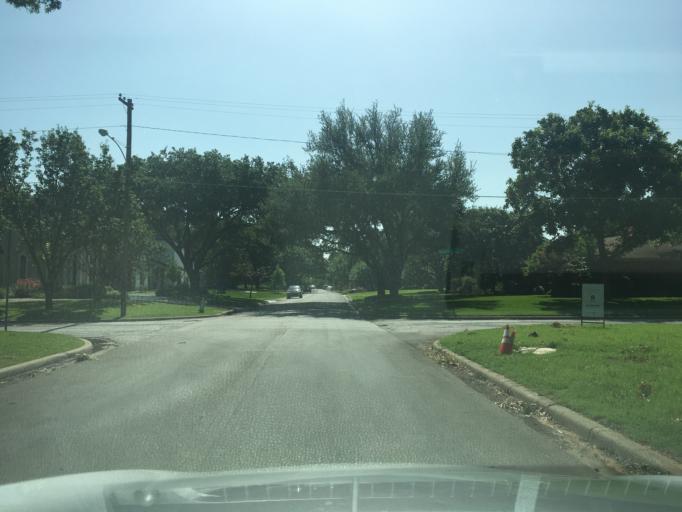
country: US
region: Texas
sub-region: Dallas County
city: Addison
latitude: 32.9075
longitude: -96.8109
